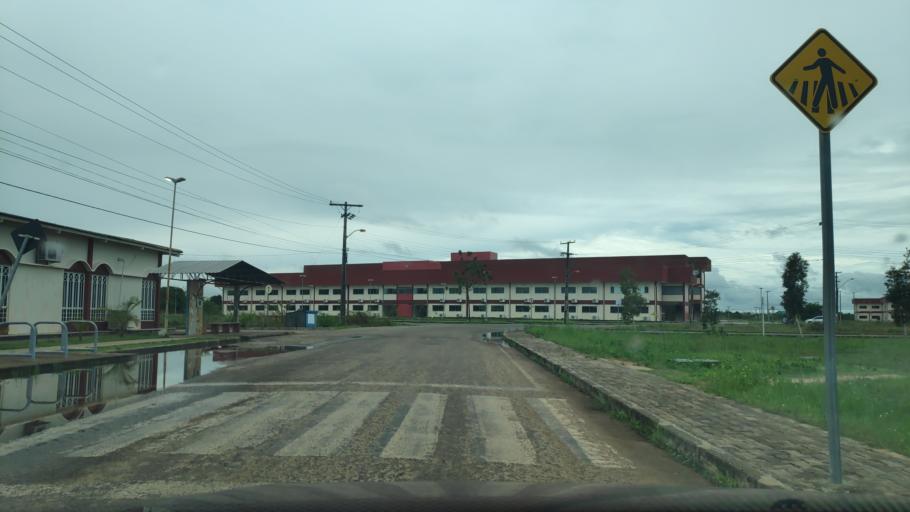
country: BR
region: Roraima
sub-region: Boa Vista
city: Boa Vista
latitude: 2.8321
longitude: -60.6982
